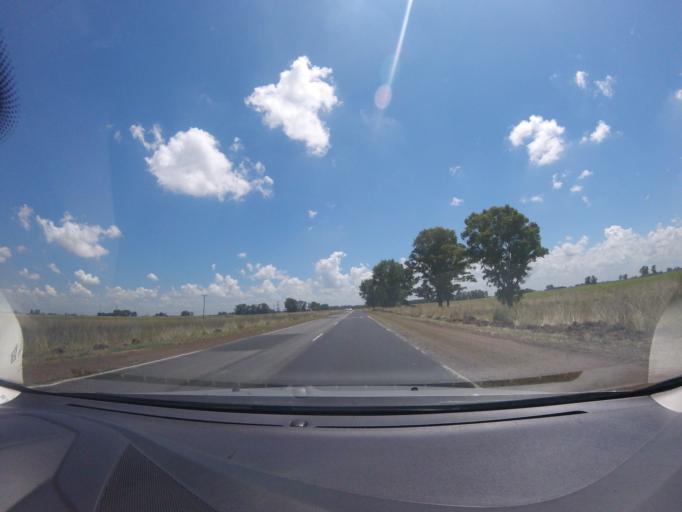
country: AR
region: Buenos Aires
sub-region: Partido de Las Flores
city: Las Flores
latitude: -36.1629
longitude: -59.0685
